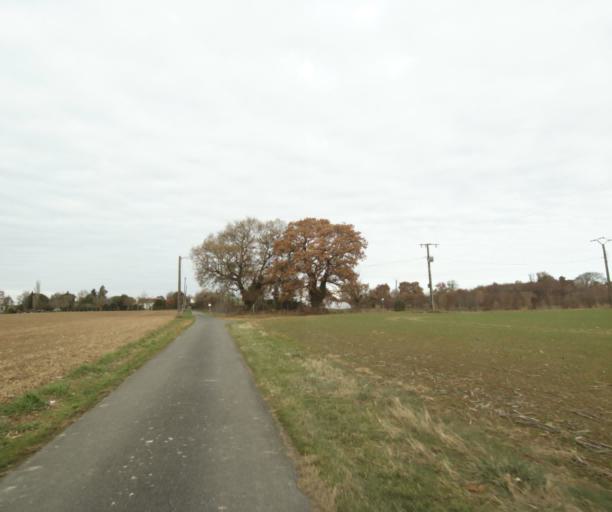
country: FR
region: Poitou-Charentes
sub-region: Departement de la Charente-Maritime
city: Corme-Royal
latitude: 45.7325
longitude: -0.7866
